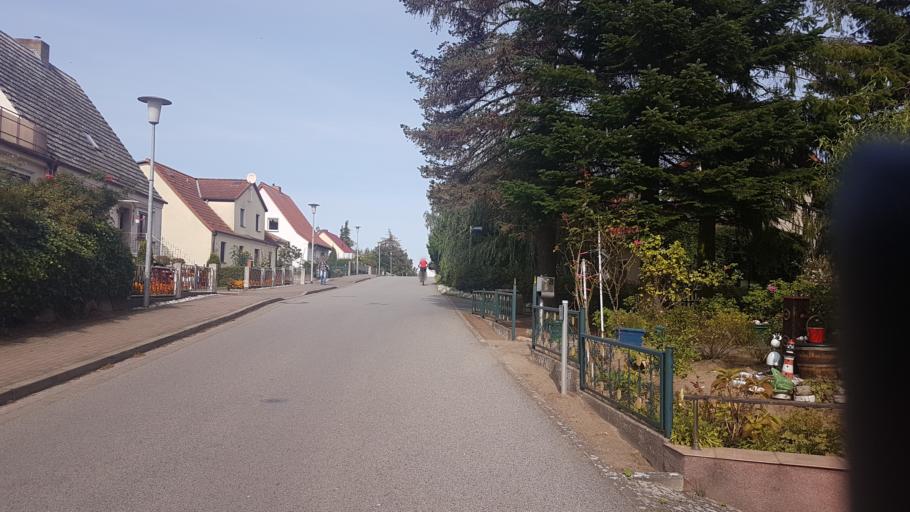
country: DE
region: Mecklenburg-Vorpommern
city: Samtens
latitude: 54.3562
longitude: 13.2898
